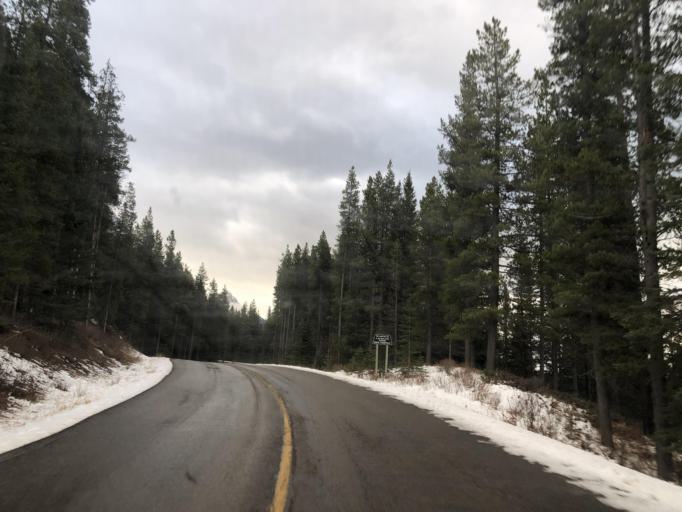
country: CA
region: Alberta
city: Canmore
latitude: 50.7121
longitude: -115.1172
